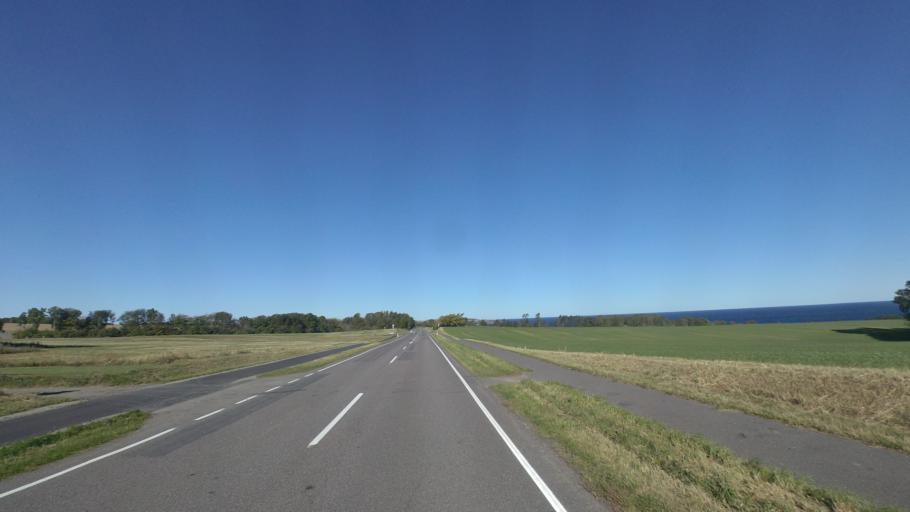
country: DK
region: Capital Region
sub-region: Bornholm Kommune
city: Nexo
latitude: 55.1654
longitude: 15.0350
